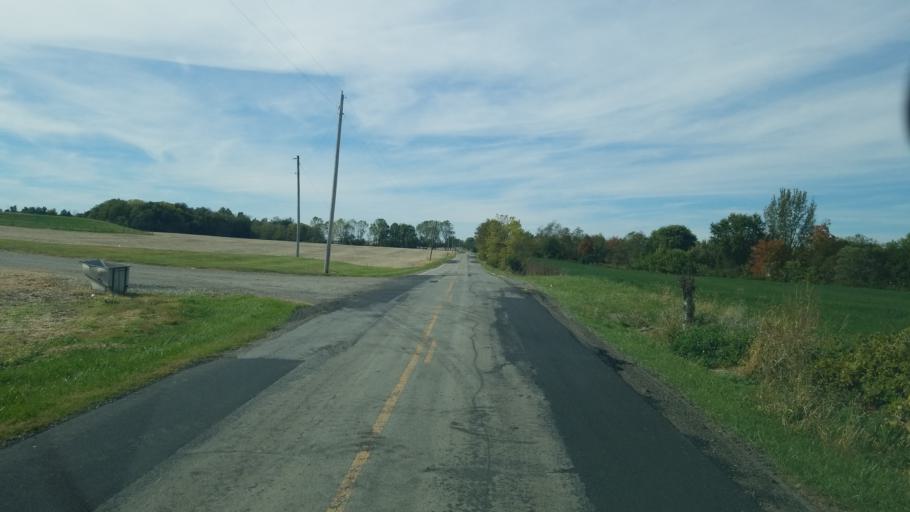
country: US
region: Ohio
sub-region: Highland County
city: Leesburg
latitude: 39.3287
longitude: -83.4876
